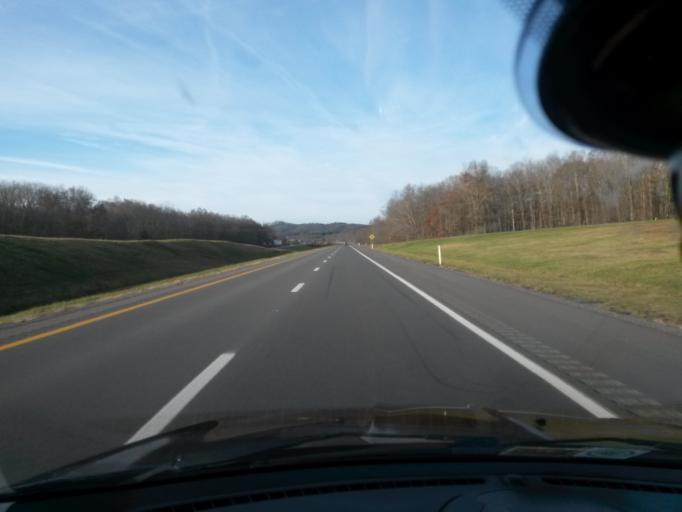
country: US
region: West Virginia
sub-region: Greenbrier County
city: Rainelle
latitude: 37.9038
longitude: -80.6339
